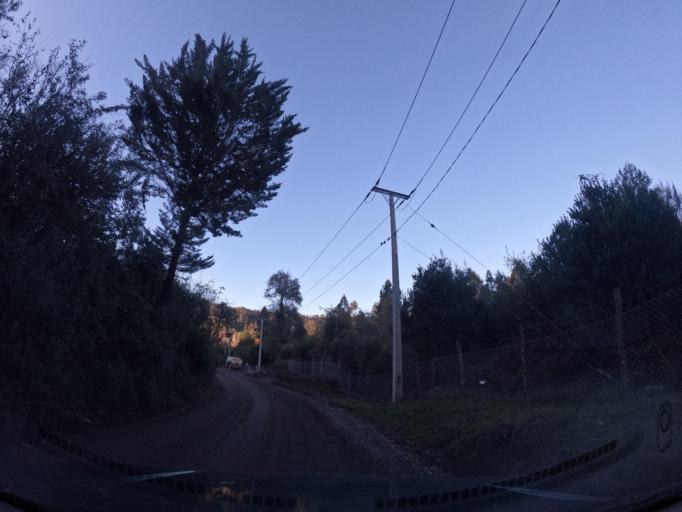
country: CL
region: Biobio
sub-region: Provincia de Concepcion
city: Chiguayante
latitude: -37.0789
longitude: -72.9365
